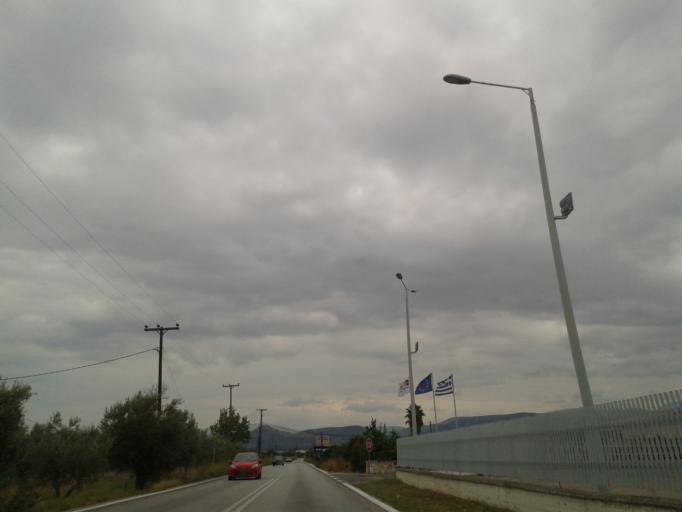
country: GR
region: Peloponnese
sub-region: Nomos Argolidos
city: Koutsopodi
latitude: 37.7056
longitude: 22.7241
